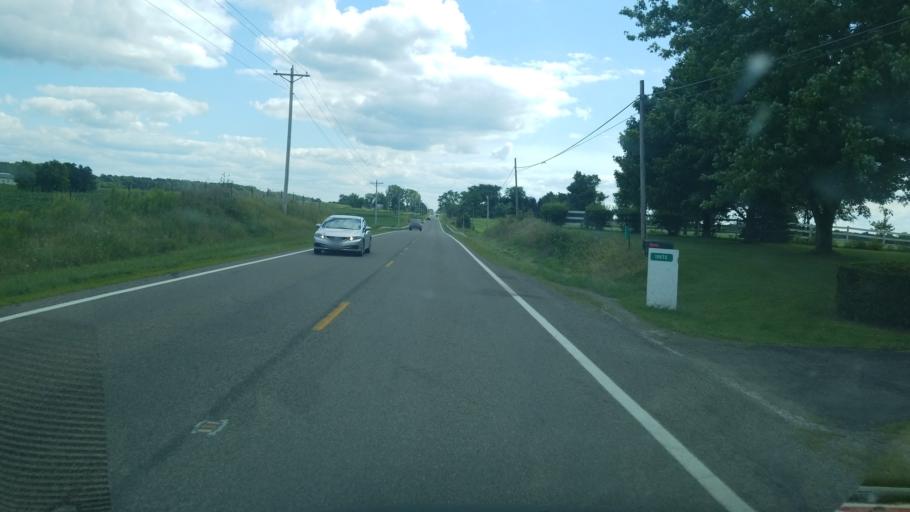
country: US
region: Ohio
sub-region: Logan County
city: Lakeview
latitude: 40.6389
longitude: -83.9756
